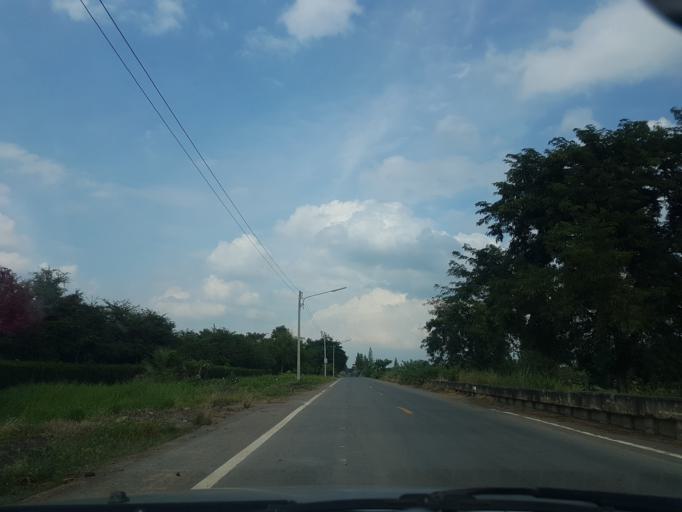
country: TH
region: Pathum Thani
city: Nong Suea
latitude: 14.2084
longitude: 100.8915
